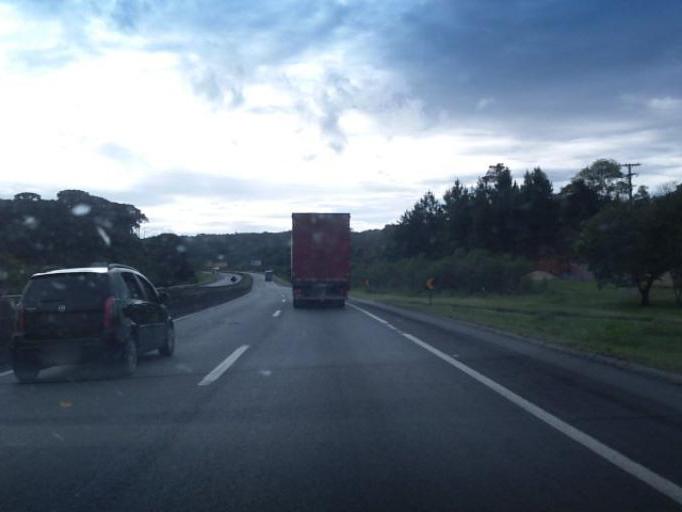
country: BR
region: Parana
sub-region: Campina Grande Do Sul
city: Campina Grande do Sul
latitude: -25.3102
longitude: -49.0094
